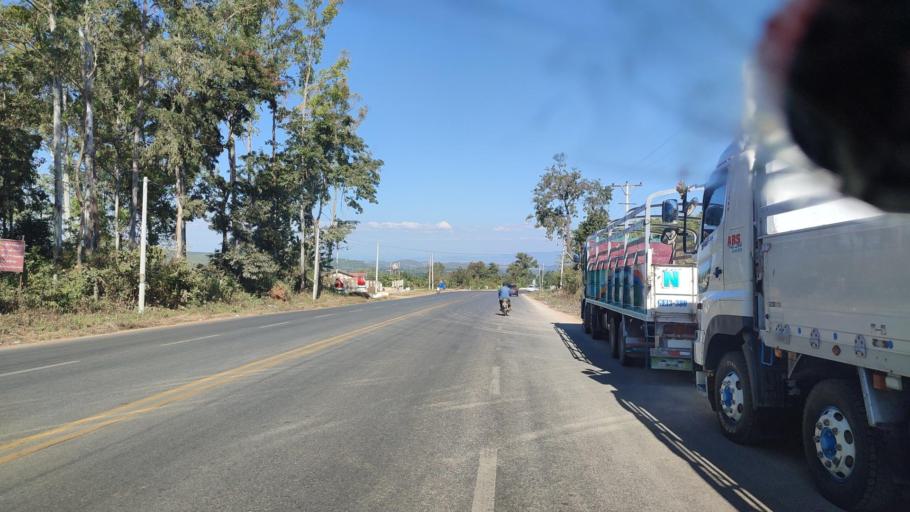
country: MM
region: Mandalay
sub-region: Pyin Oo Lwin District
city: Pyin Oo Lwin
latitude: 22.0665
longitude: 96.5736
